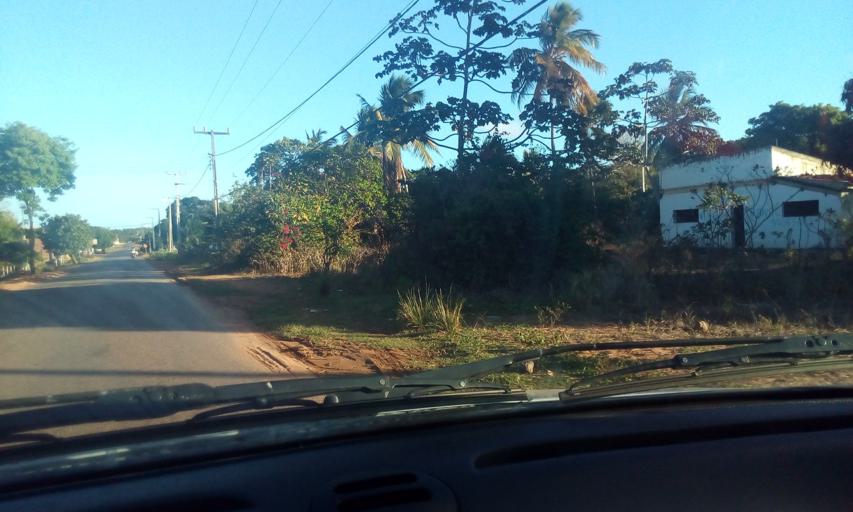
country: BR
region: Rio Grande do Norte
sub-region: Parnamirim
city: Parnamirim
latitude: -5.9522
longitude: -35.1758
